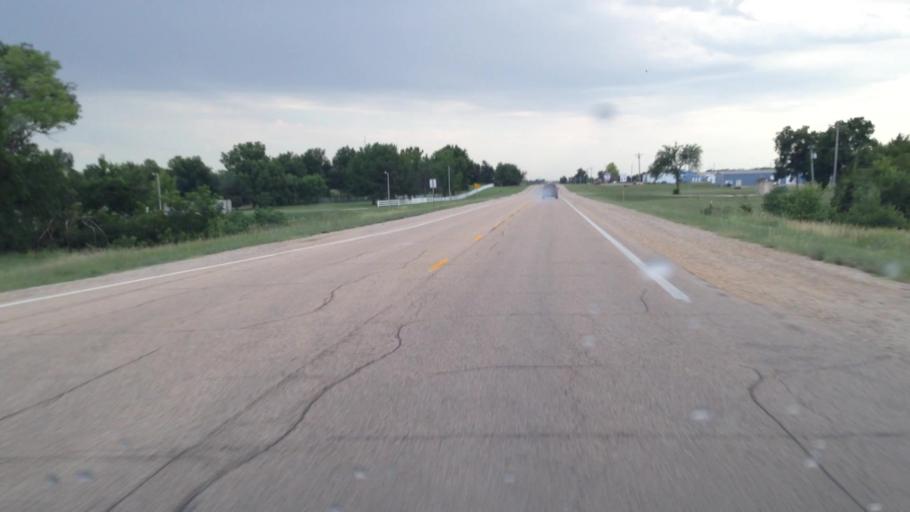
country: US
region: Kansas
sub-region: Coffey County
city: Burlington
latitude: 38.1830
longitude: -95.7388
